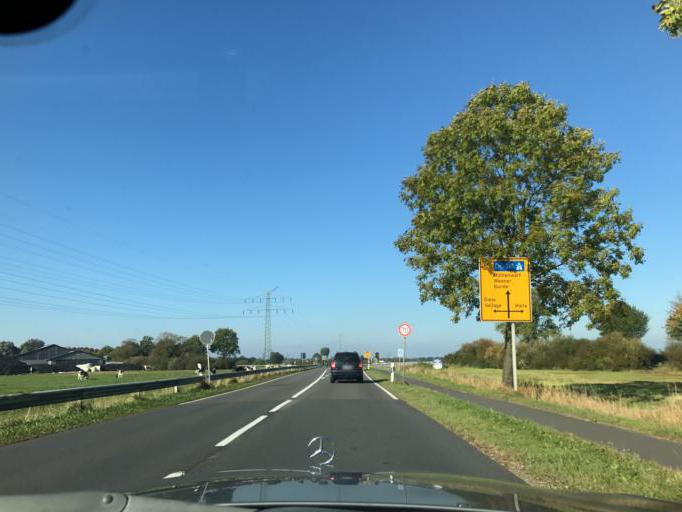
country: DE
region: Lower Saxony
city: Weener
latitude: 53.1116
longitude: 7.3472
